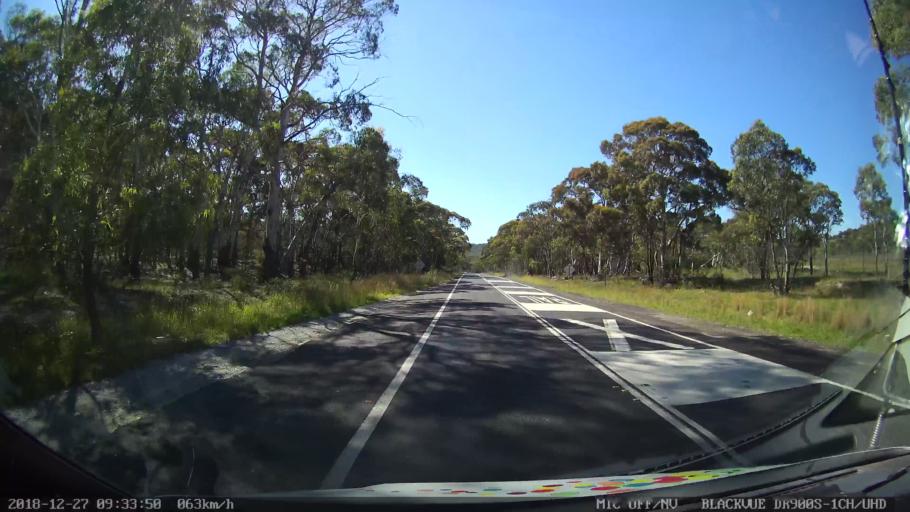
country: AU
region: New South Wales
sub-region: Lithgow
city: Portland
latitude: -33.2199
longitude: 150.0237
